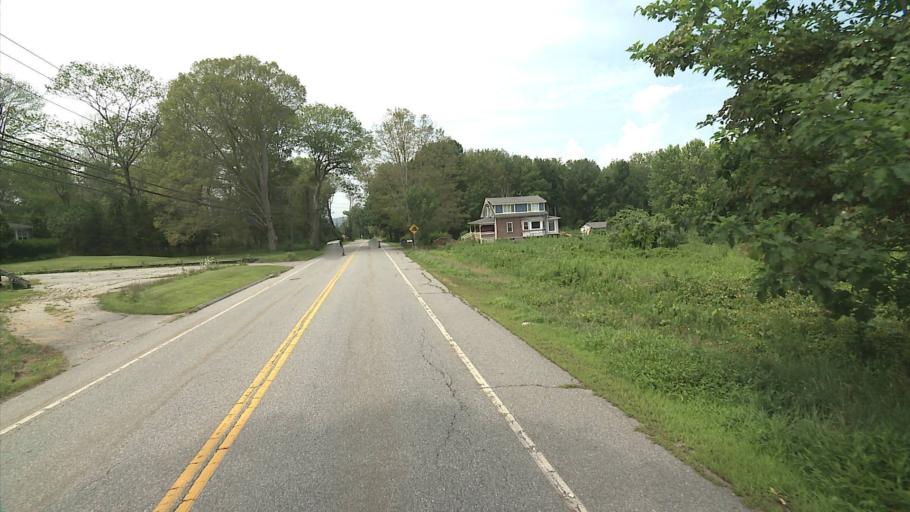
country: US
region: Connecticut
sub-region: Windham County
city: Danielson
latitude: 41.8086
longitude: -71.8661
